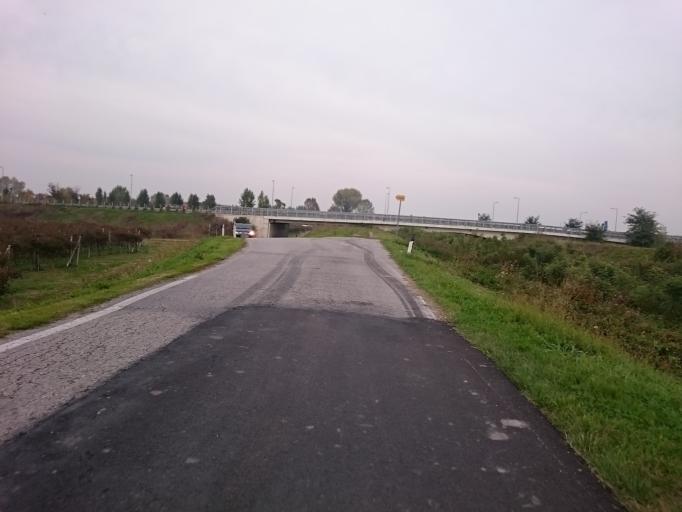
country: IT
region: Veneto
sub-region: Provincia di Padova
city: Terradura
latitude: 45.3157
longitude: 11.8040
